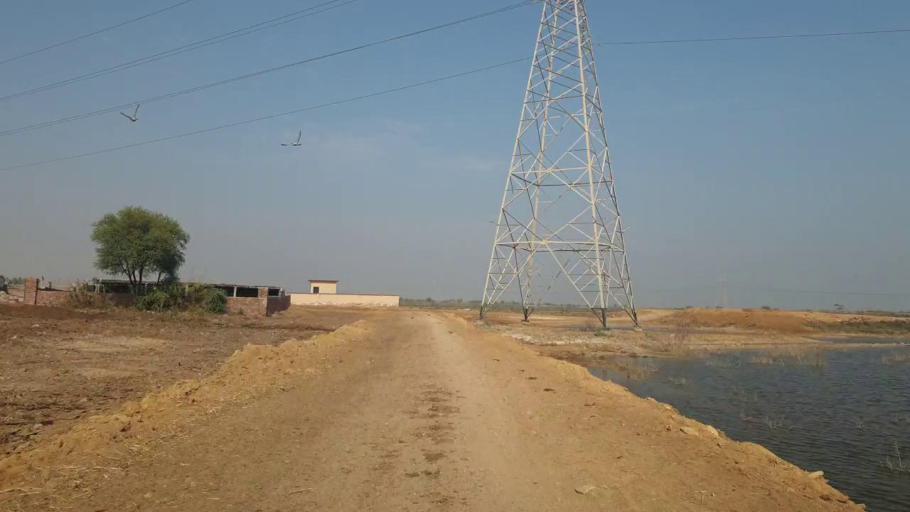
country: PK
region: Sindh
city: Jamshoro
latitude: 25.4631
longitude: 68.2935
